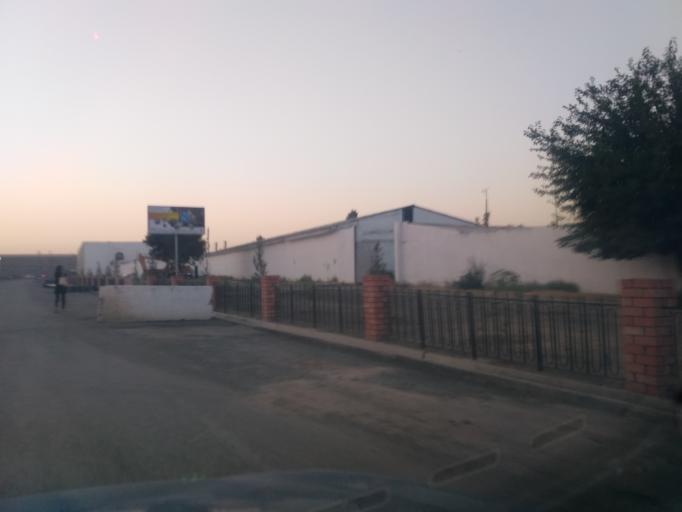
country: UZ
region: Sirdaryo
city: Guliston
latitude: 40.5058
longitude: 68.7679
